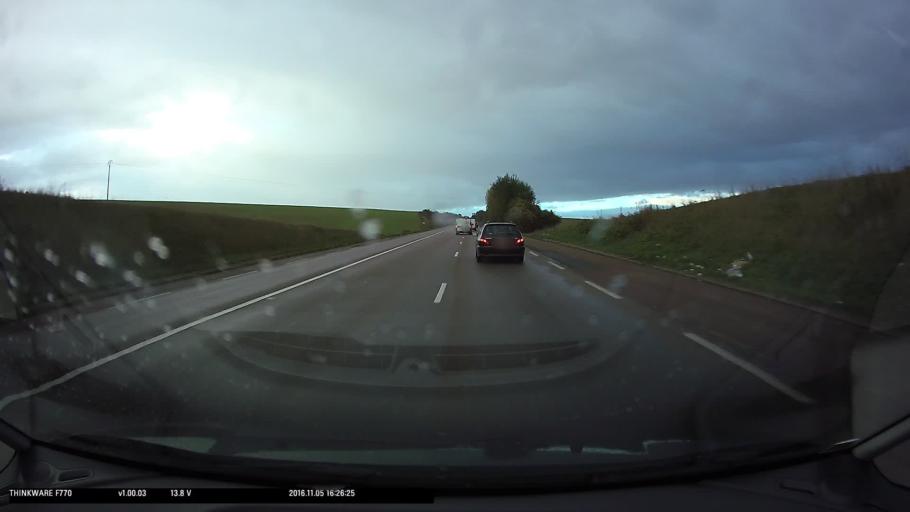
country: FR
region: Ile-de-France
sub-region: Departement des Yvelines
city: Meulan-en-Yvelines
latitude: 49.0193
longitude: 1.9100
